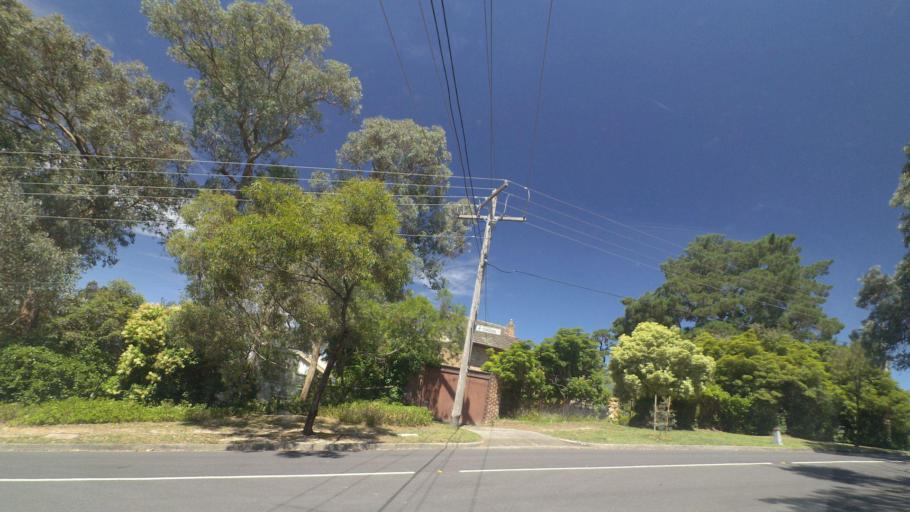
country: AU
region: Victoria
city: Mitcham
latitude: -37.8045
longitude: 145.2237
